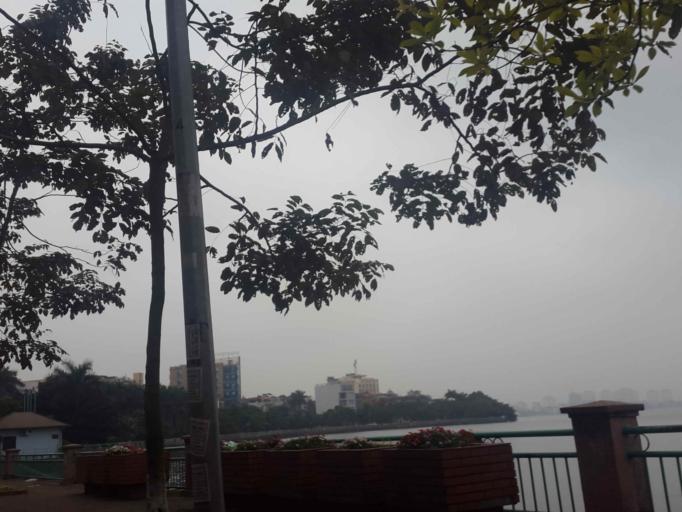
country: VN
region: Ha Noi
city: Cau Giay
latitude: 21.0453
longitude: 105.8162
